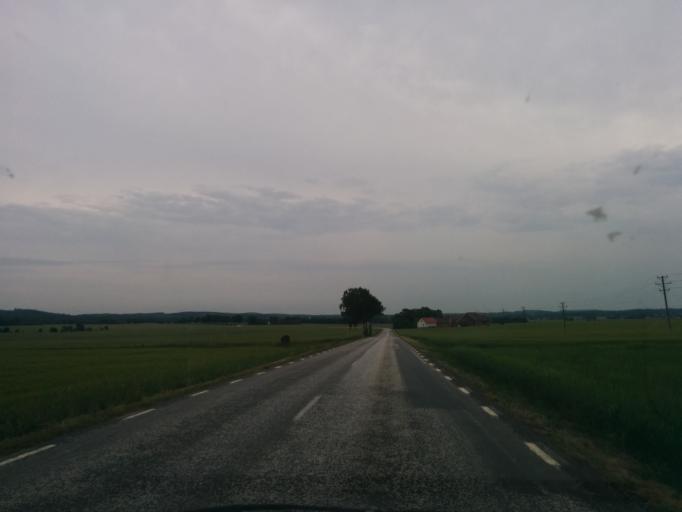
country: SE
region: Skane
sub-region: Lunds Kommun
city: Genarp
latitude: 55.6322
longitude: 13.3757
